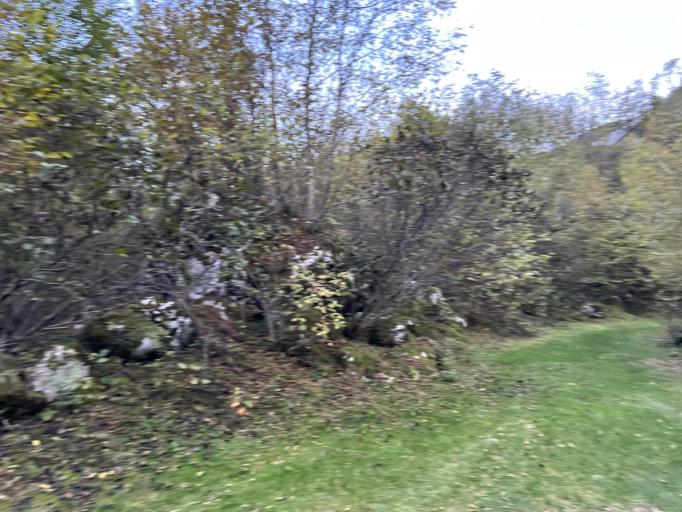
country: SI
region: Tolmin
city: Tolmin
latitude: 46.2380
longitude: 13.7232
